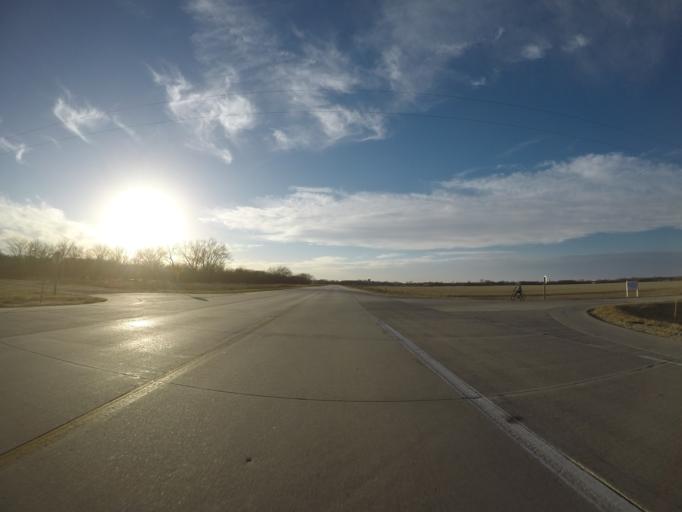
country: US
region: Kansas
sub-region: Chase County
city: Cottonwood Falls
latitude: 38.4069
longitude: -96.3730
